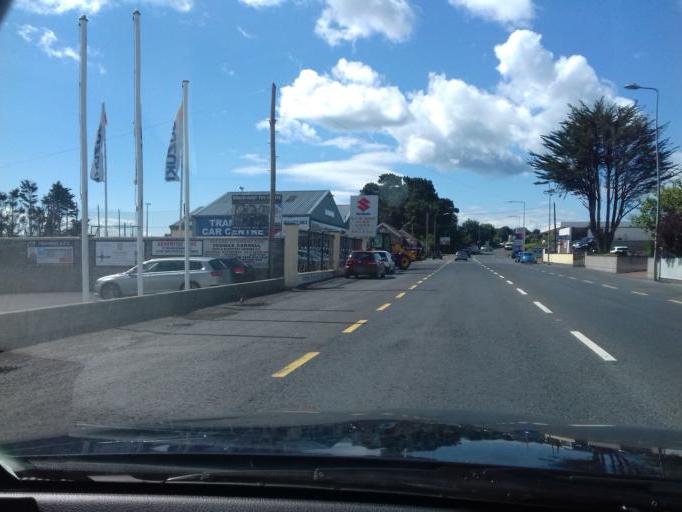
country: IE
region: Munster
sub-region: Waterford
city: Tra Mhor
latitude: 52.1712
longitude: -7.1411
